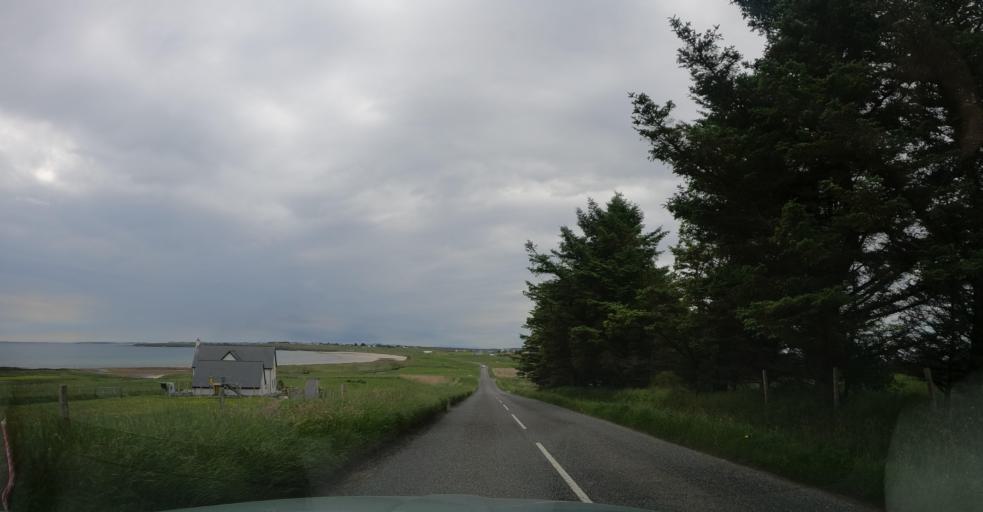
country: GB
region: Scotland
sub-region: Eilean Siar
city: Isle of Lewis
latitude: 58.2721
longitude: -6.3163
